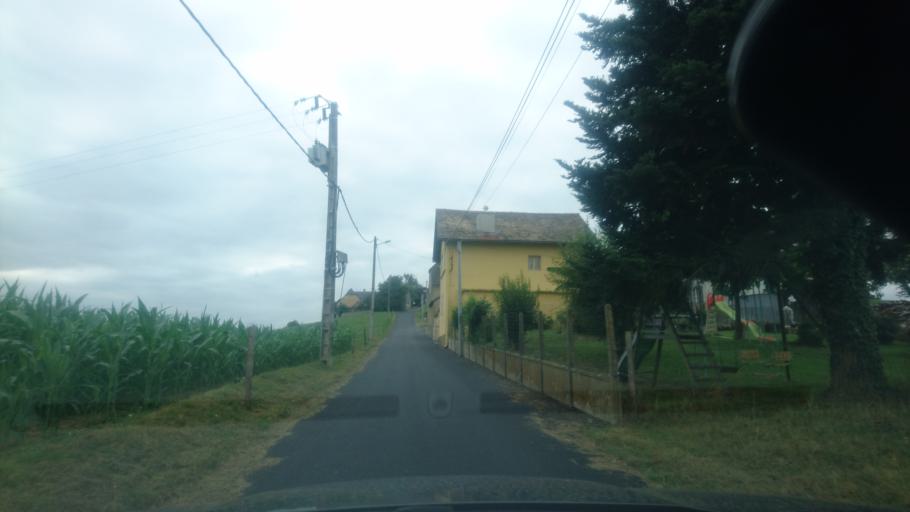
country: FR
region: Midi-Pyrenees
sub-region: Departement des Hautes-Pyrenees
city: Horgues
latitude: 43.1220
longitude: 0.0645
